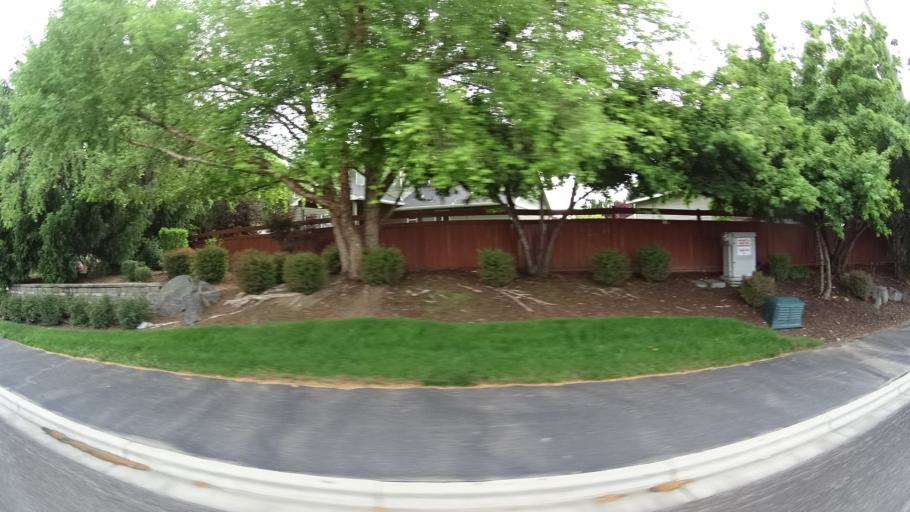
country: US
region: Idaho
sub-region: Ada County
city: Meridian
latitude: 43.5992
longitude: -116.3745
